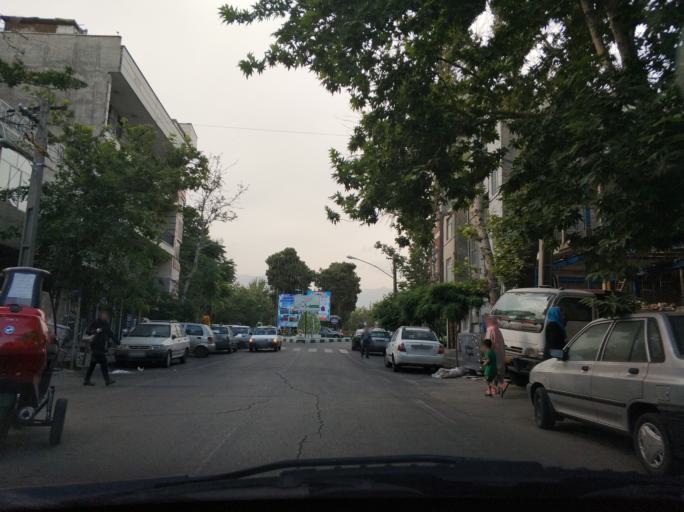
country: IR
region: Tehran
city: Tehran
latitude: 35.7174
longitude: 51.4744
